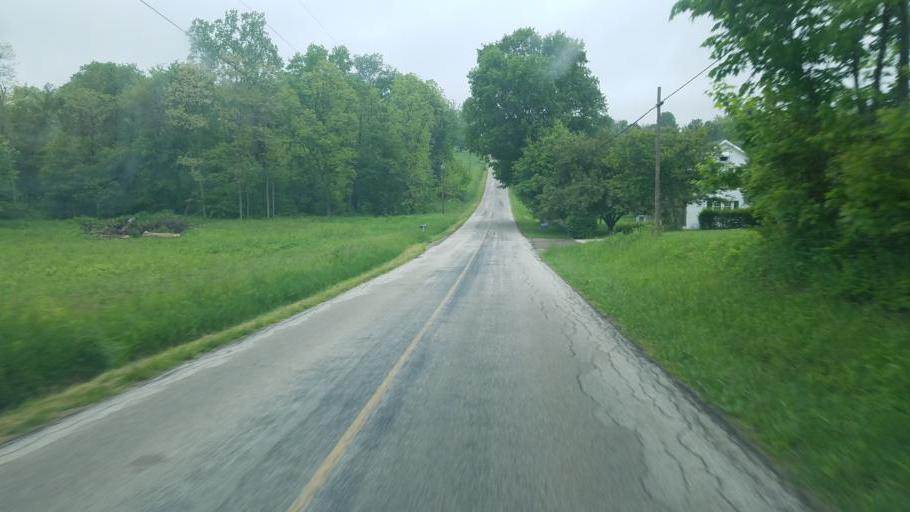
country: US
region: Ohio
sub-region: Sandusky County
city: Bellville
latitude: 40.6781
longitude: -82.4728
